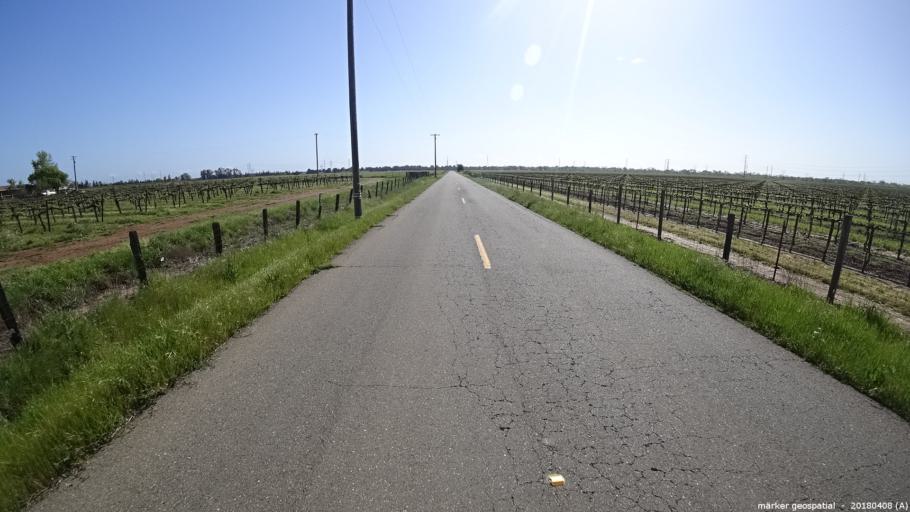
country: US
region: California
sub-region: Sacramento County
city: Elk Grove
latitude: 38.3617
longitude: -121.3644
